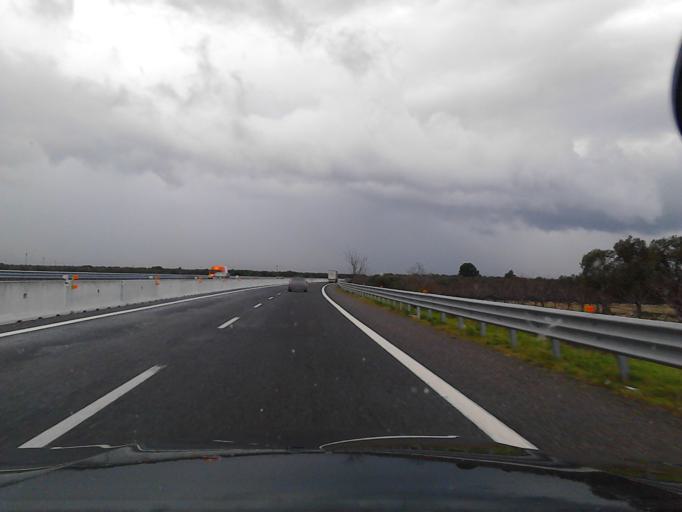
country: IT
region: Apulia
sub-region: Provincia di Bari
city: Modugno
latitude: 41.1019
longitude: 16.7512
